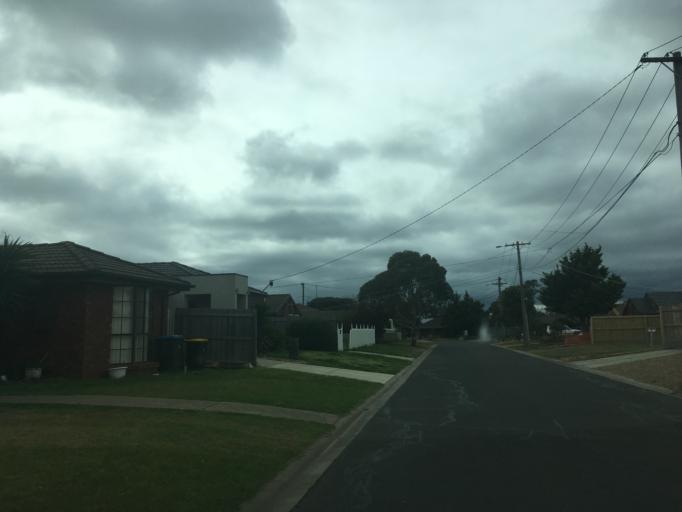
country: AU
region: Victoria
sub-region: Wyndham
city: Hoppers Crossing
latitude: -37.8668
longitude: 144.7087
